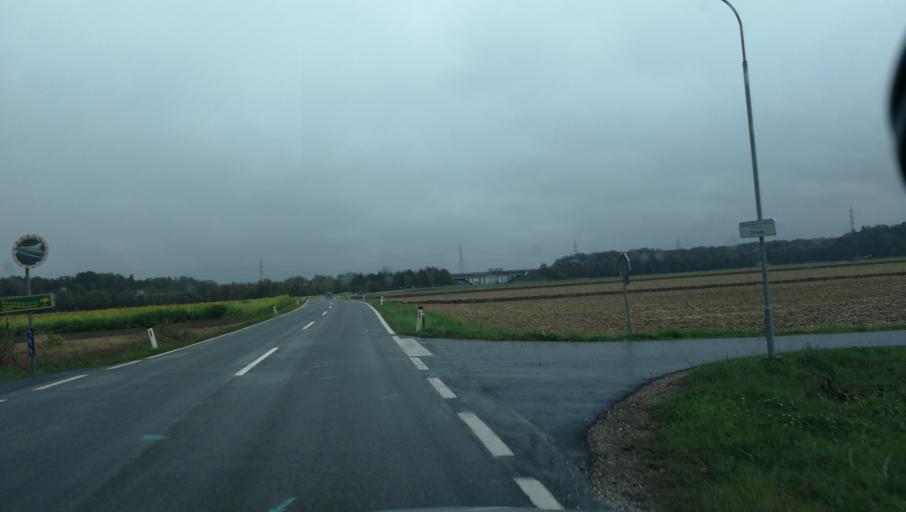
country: AT
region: Styria
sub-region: Politischer Bezirk Leibnitz
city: Strass in Steiermark
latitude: 46.7256
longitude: 15.6398
